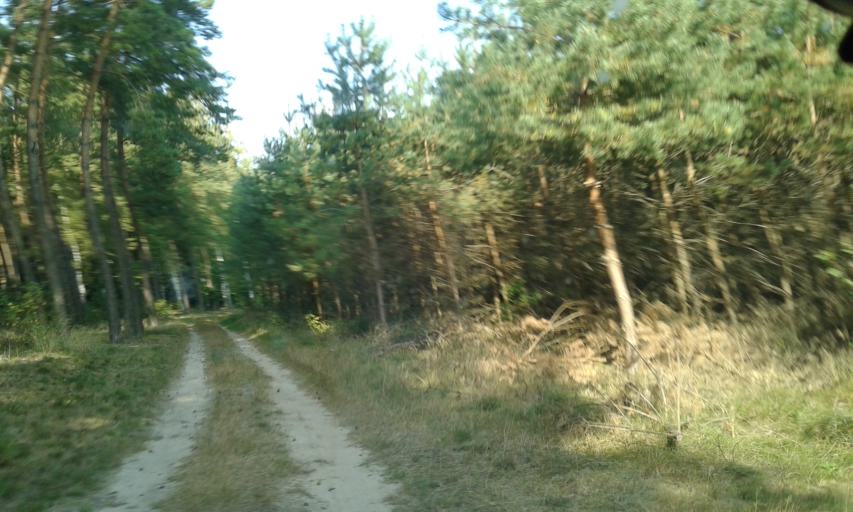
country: PL
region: West Pomeranian Voivodeship
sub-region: Powiat stargardzki
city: Suchan
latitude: 53.2458
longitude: 15.3624
